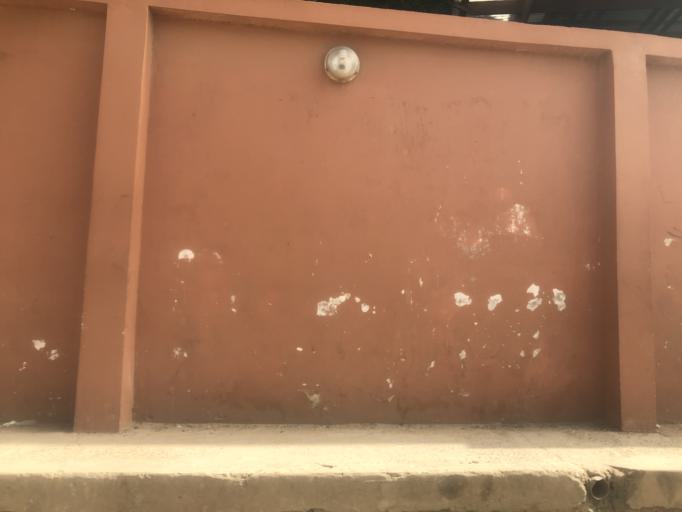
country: SN
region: Dakar
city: Mermoz Boabab
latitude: 14.7370
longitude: -17.5088
